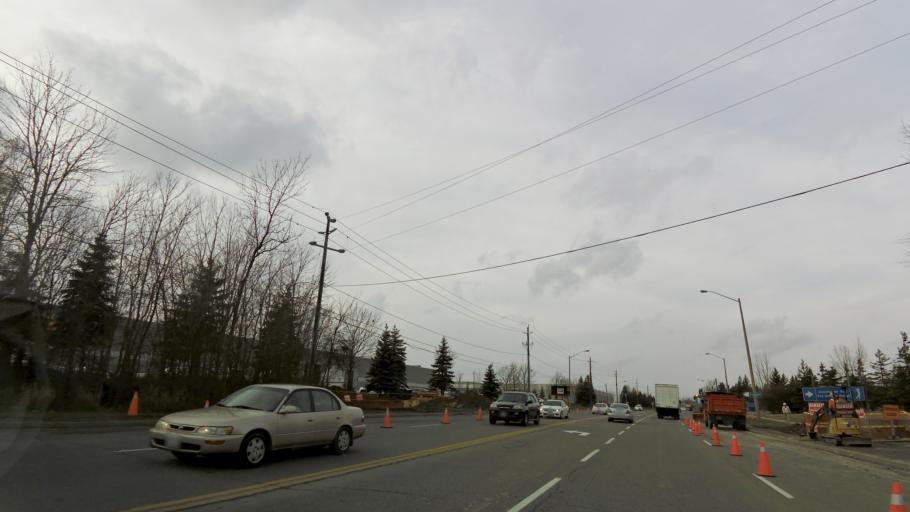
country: CA
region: Ontario
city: Etobicoke
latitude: 43.7388
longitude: -79.6418
